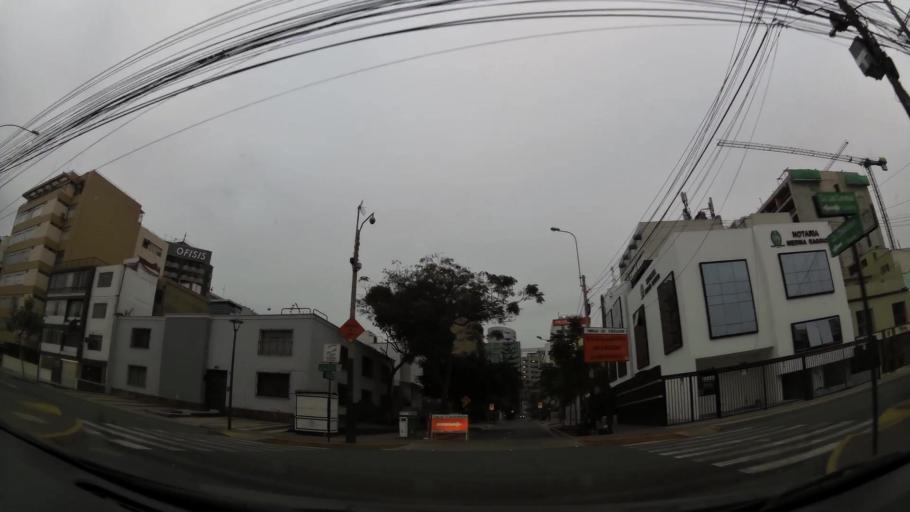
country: PE
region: Lima
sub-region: Lima
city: San Isidro
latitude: -12.0957
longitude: -77.0289
